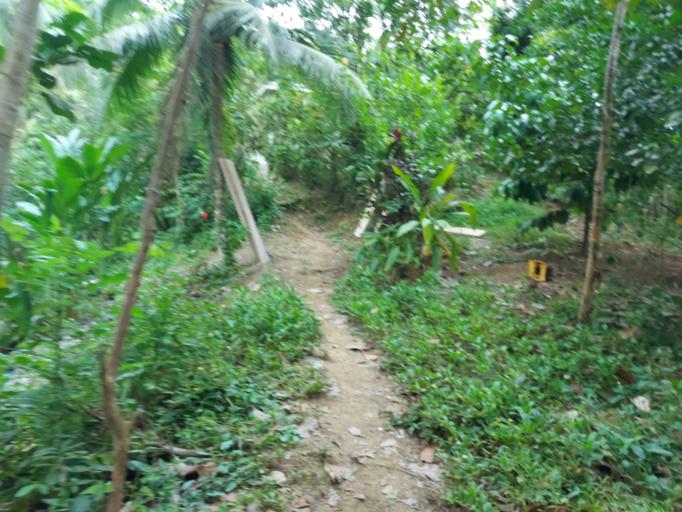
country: PA
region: Bocas del Toro
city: Barranco
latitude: 9.6395
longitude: -82.7829
